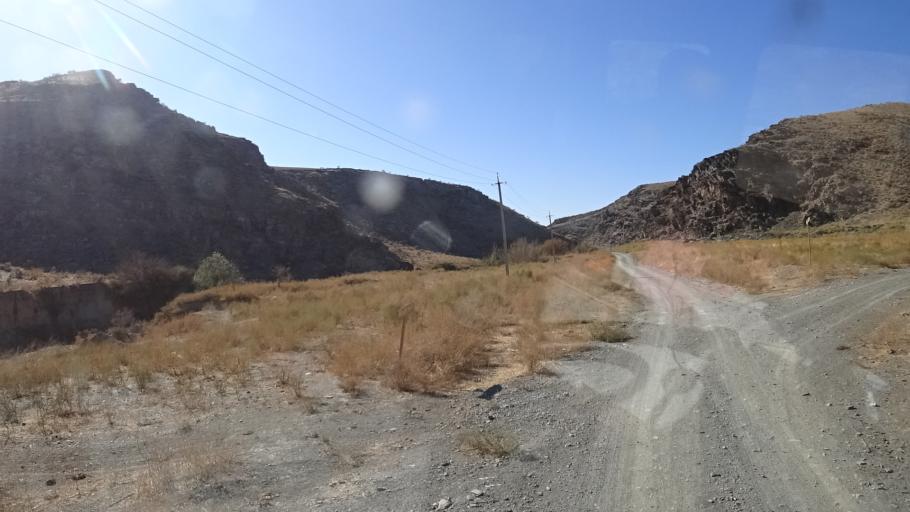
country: UZ
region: Navoiy
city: Nurota
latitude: 40.3117
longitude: 65.6245
